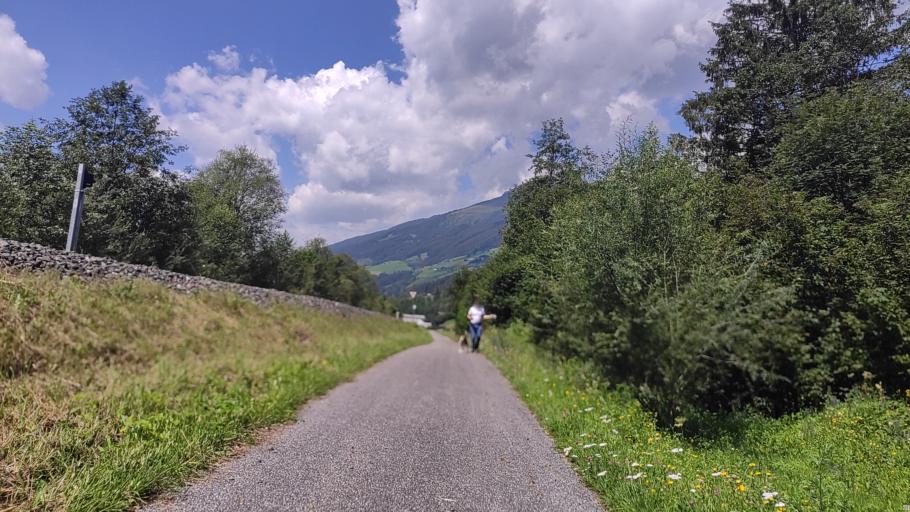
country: AT
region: Salzburg
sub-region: Politischer Bezirk Zell am See
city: Neukirchen am Grossvenediger
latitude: 47.2437
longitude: 12.2565
